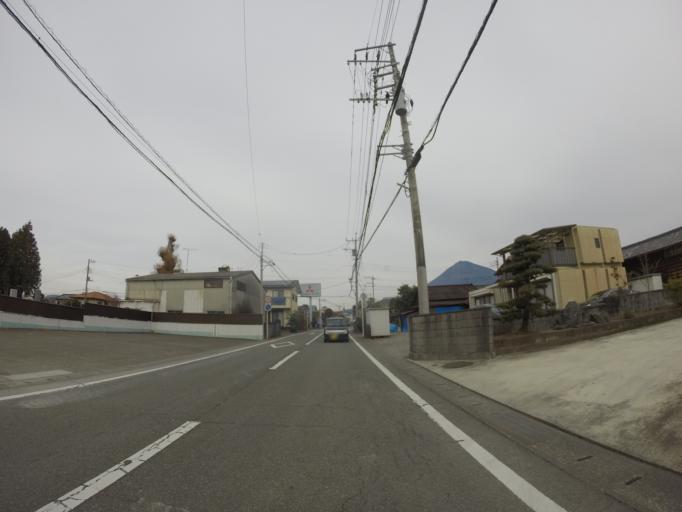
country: JP
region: Shizuoka
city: Fujinomiya
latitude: 35.2257
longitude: 138.6191
